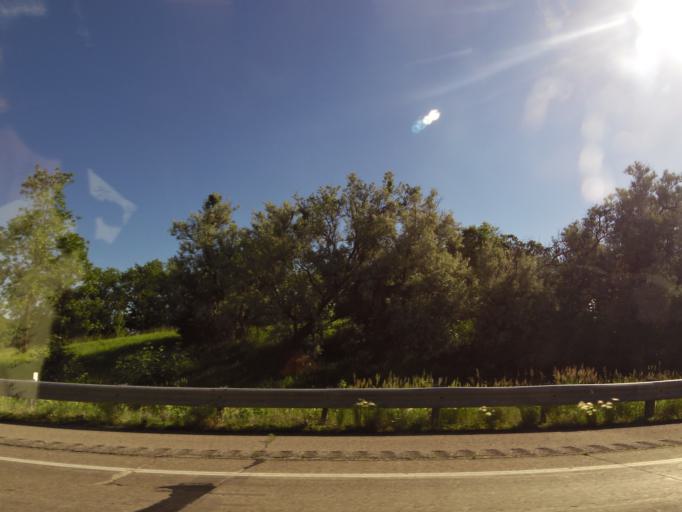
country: US
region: Minnesota
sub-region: Grant County
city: Elbow Lake
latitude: 46.0764
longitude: -95.8733
